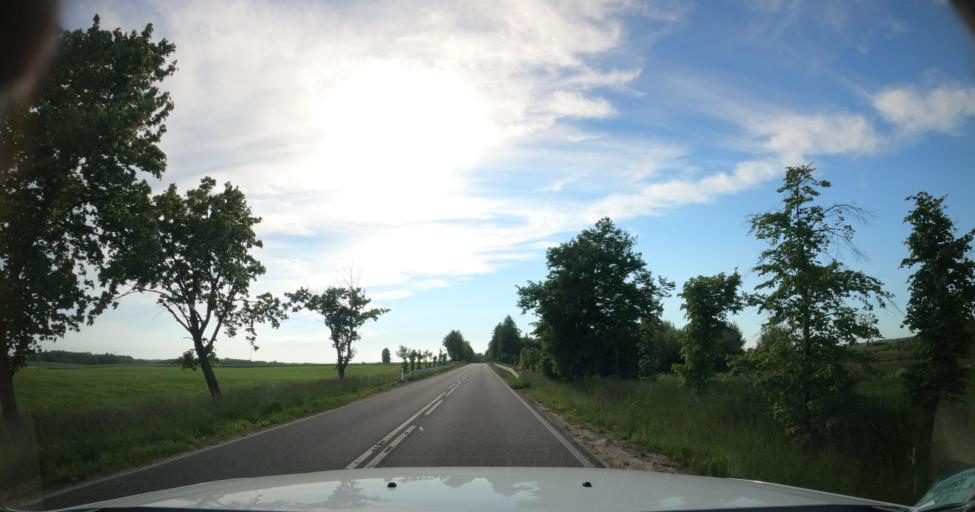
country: PL
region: Warmian-Masurian Voivodeship
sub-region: Powiat ostrodzki
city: Morag
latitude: 54.0817
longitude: 19.8943
